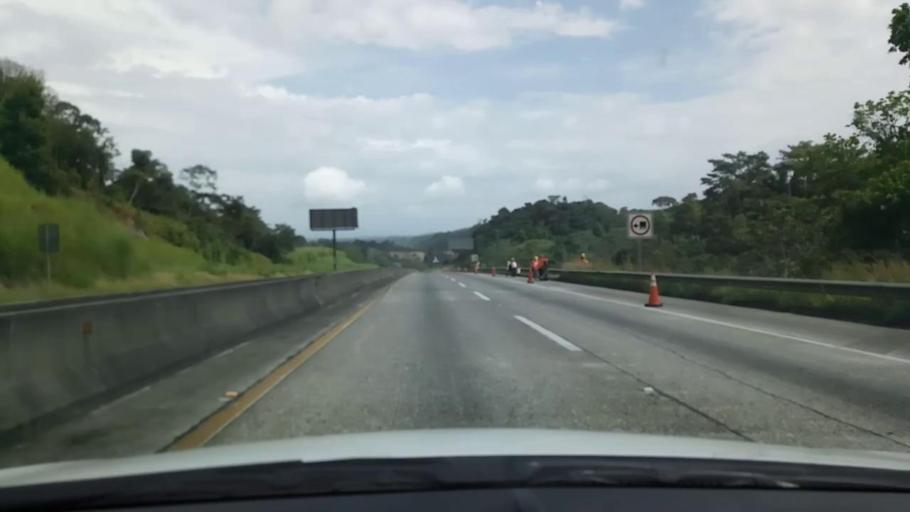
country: PA
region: Colon
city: Quebrada Bonita Adentro
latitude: 9.2825
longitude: -79.7328
